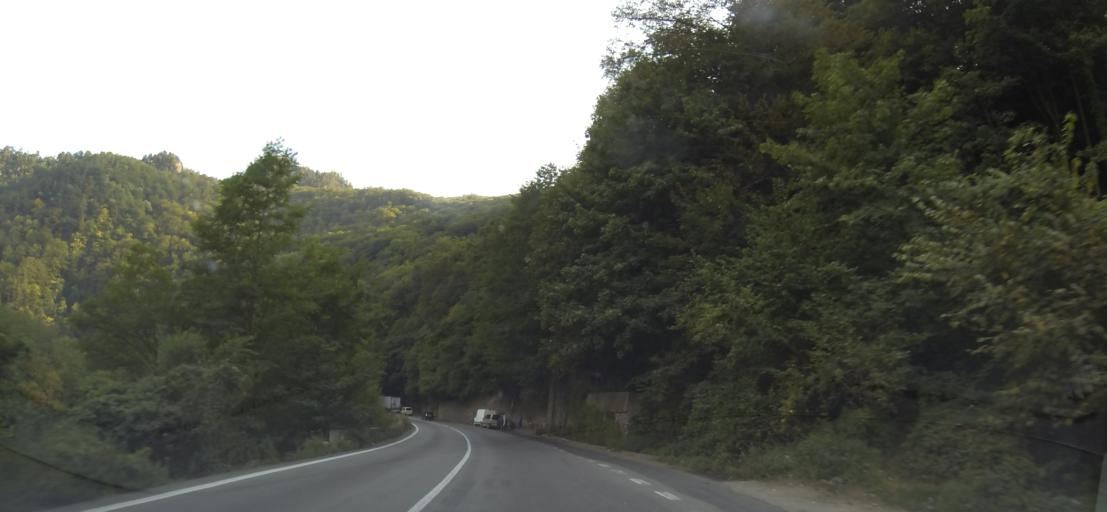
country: RO
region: Valcea
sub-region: Comuna Brezoi
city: Brezoi
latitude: 45.3104
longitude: 24.2689
